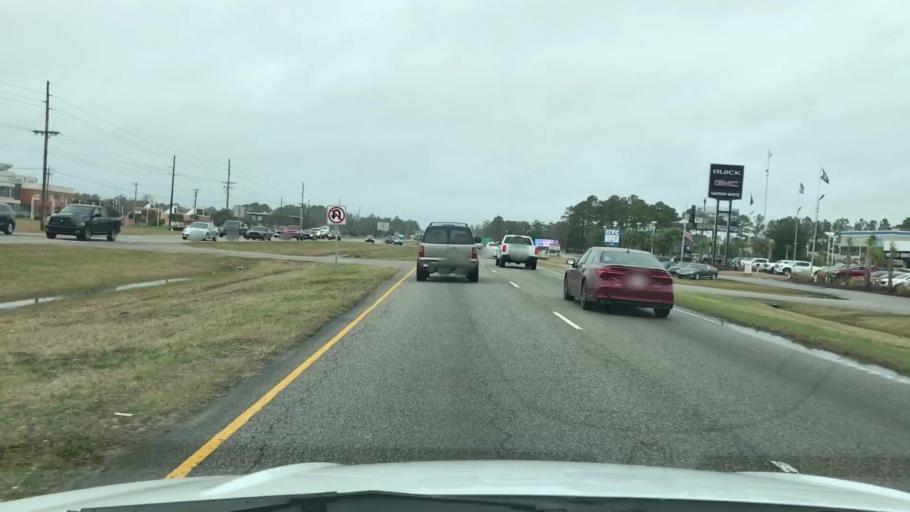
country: US
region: South Carolina
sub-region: Horry County
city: Red Hill
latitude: 33.7933
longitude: -78.9991
